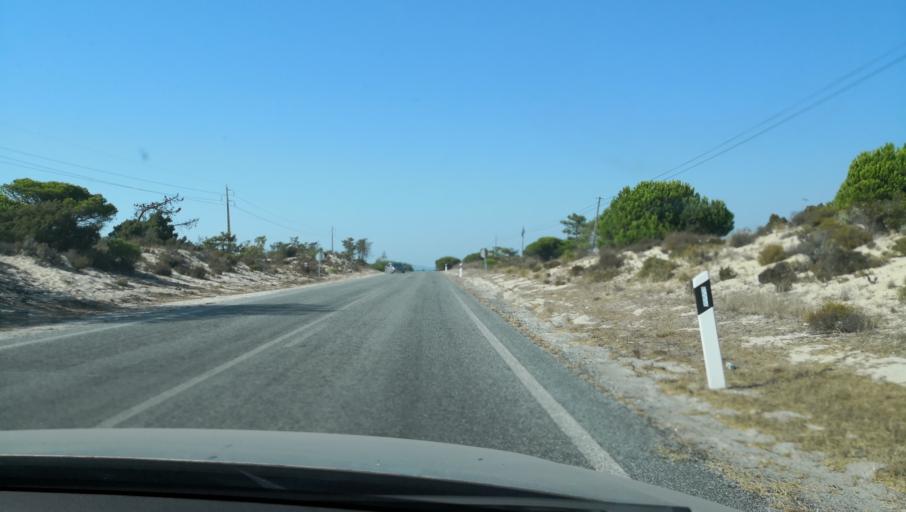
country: PT
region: Setubal
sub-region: Setubal
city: Setubal
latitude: 38.4203
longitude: -8.8206
